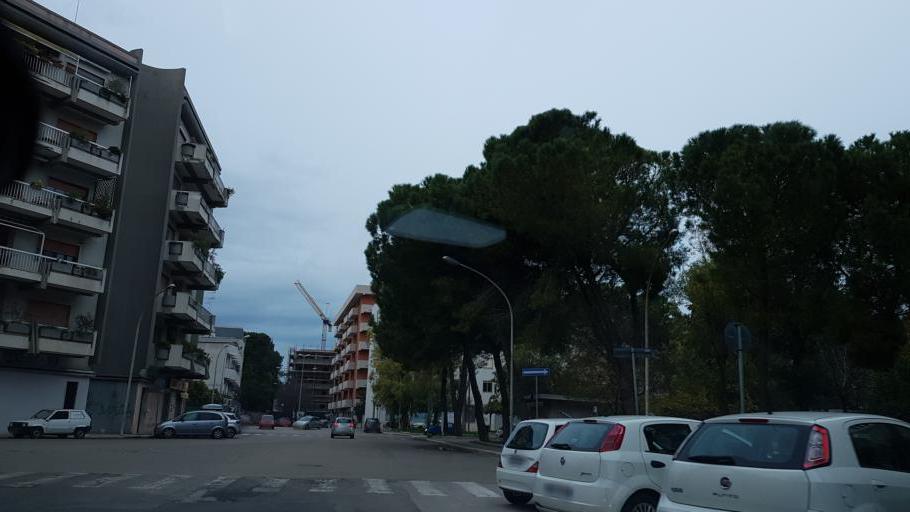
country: IT
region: Apulia
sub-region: Provincia di Brindisi
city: Brindisi
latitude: 40.6269
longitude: 17.9247
